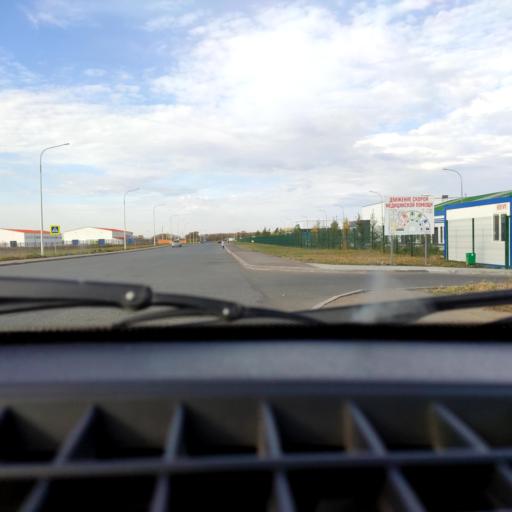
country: RU
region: Bashkortostan
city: Ufa
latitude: 54.6027
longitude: 55.9101
